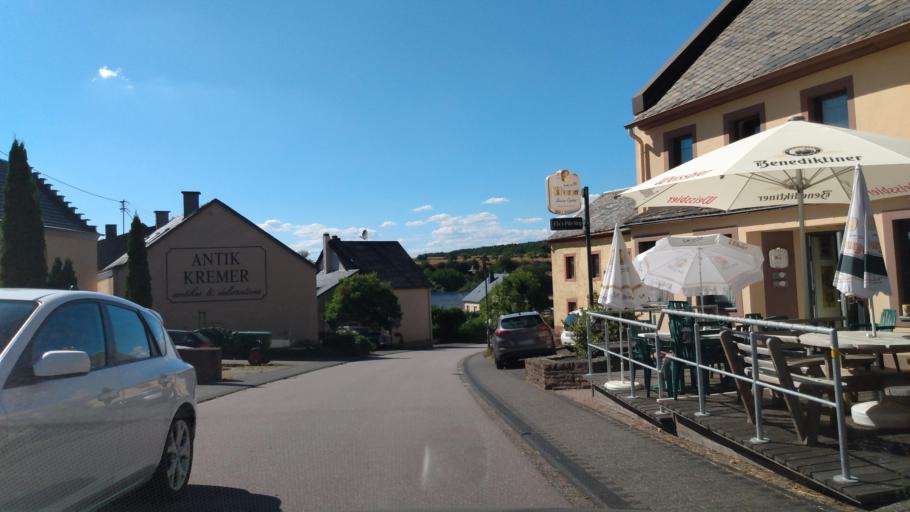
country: DE
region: Rheinland-Pfalz
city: Spangdahlem
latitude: 49.9804
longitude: 6.6817
